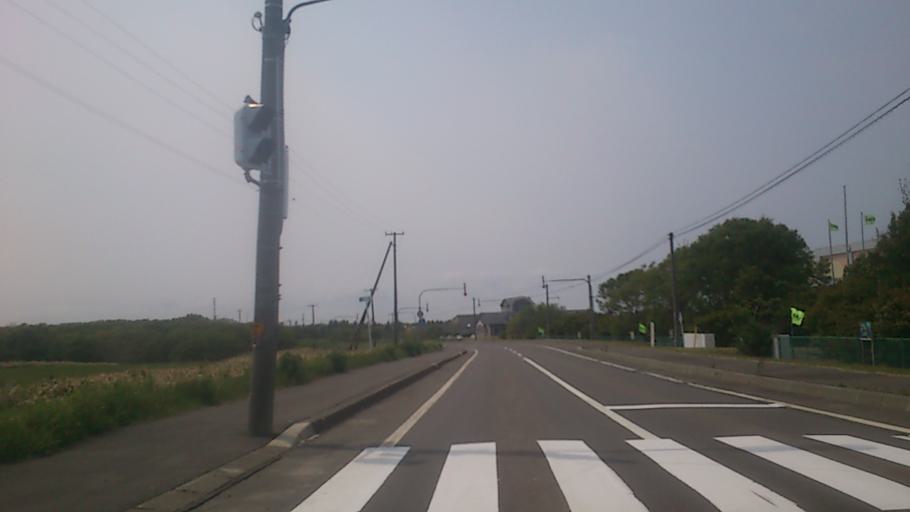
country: JP
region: Hokkaido
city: Nemuro
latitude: 43.2785
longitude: 145.5195
